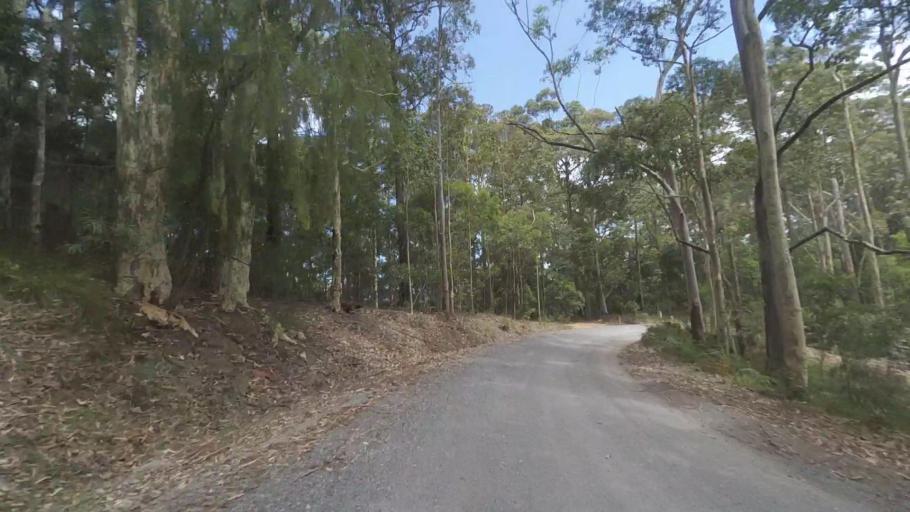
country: AU
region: New South Wales
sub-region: Shoalhaven Shire
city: Milton
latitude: -35.4424
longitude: 150.2959
